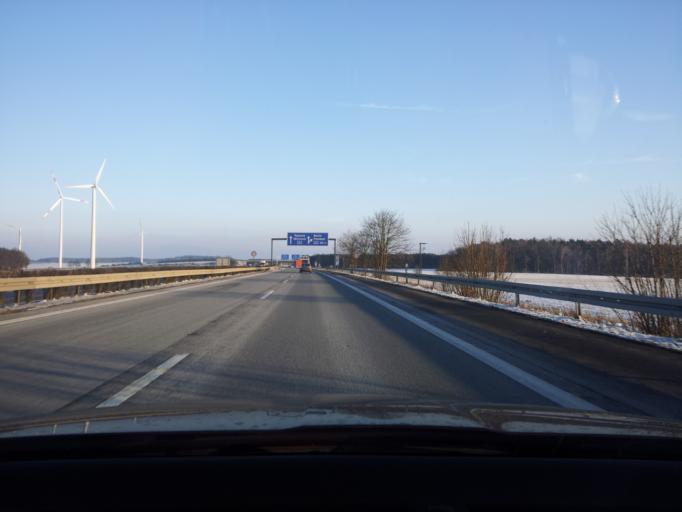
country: DE
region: Brandenburg
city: Wittstock
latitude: 53.1370
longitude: 12.4383
